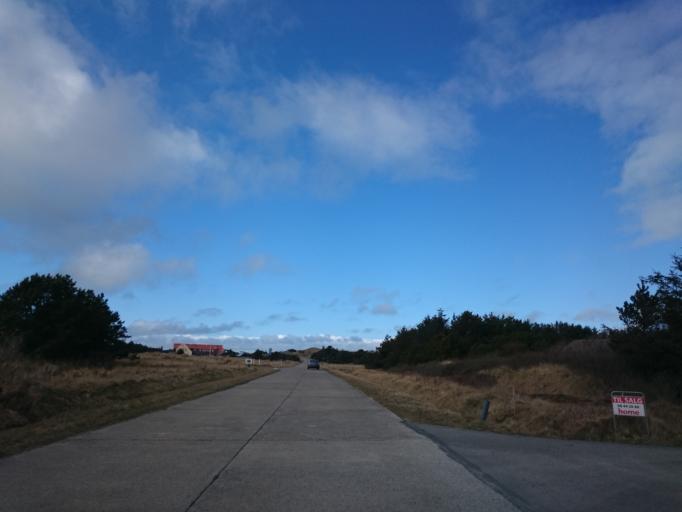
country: DK
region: North Denmark
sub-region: Frederikshavn Kommune
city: Strandby
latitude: 57.6611
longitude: 10.3964
